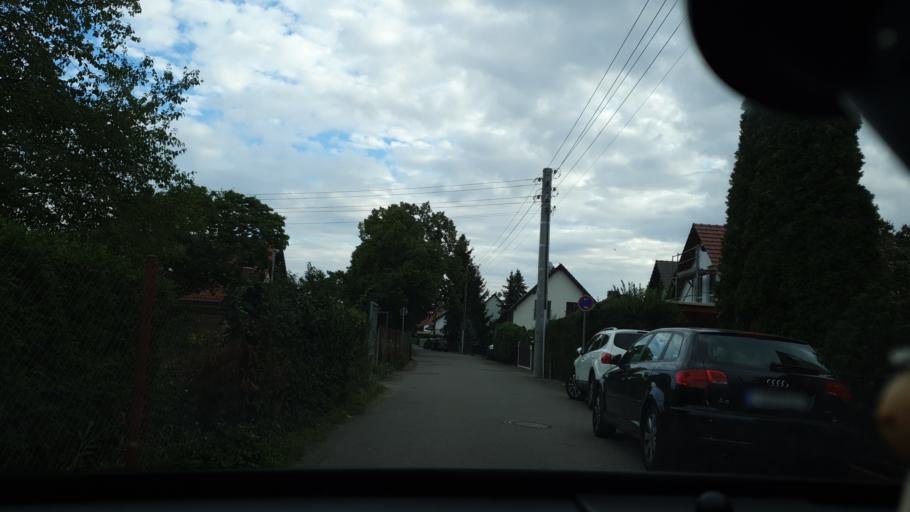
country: DE
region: Saxony
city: Torgau
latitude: 51.5504
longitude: 12.9926
